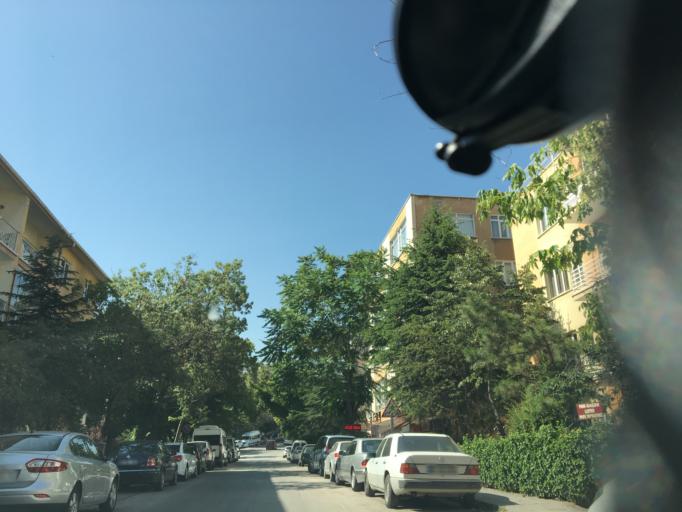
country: TR
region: Ankara
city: Ankara
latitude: 39.9041
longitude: 32.8498
